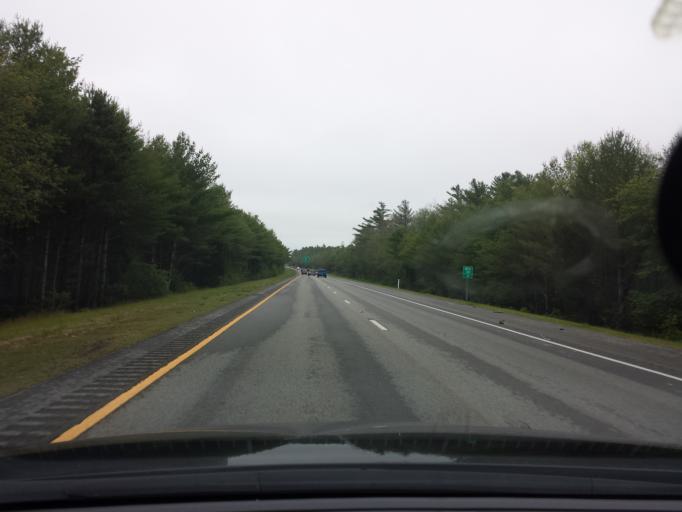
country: US
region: Massachusetts
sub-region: Plymouth County
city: Marion Center
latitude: 41.7137
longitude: -70.7878
